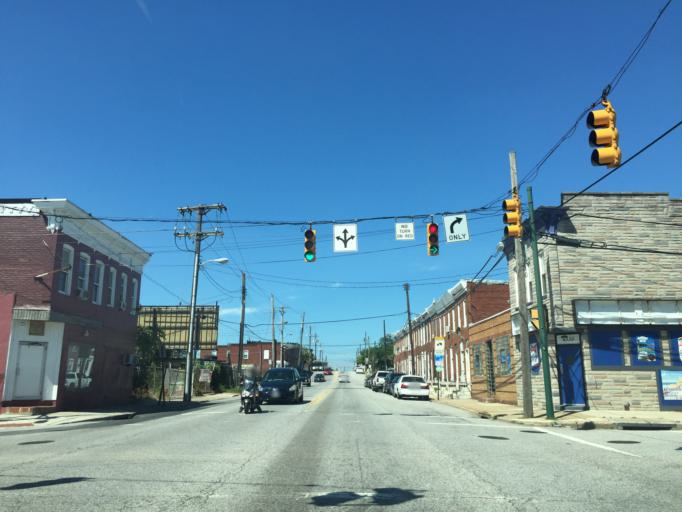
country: US
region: Maryland
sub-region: City of Baltimore
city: Baltimore
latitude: 39.2917
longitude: -76.5597
